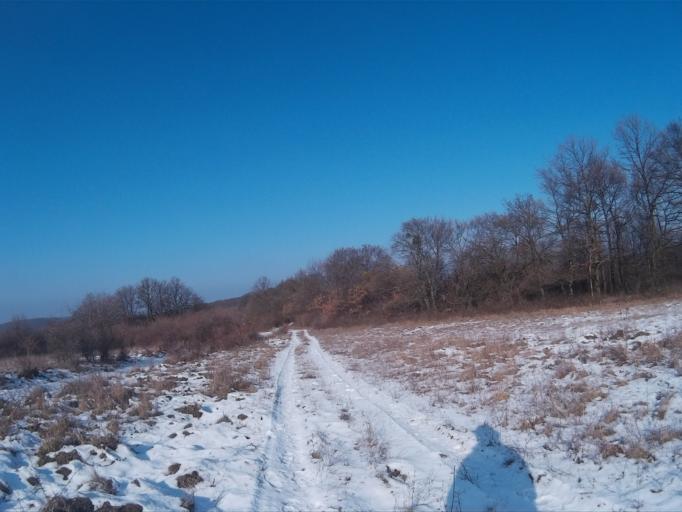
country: HU
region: Komarom-Esztergom
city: Labatlan
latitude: 47.7131
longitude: 18.4946
